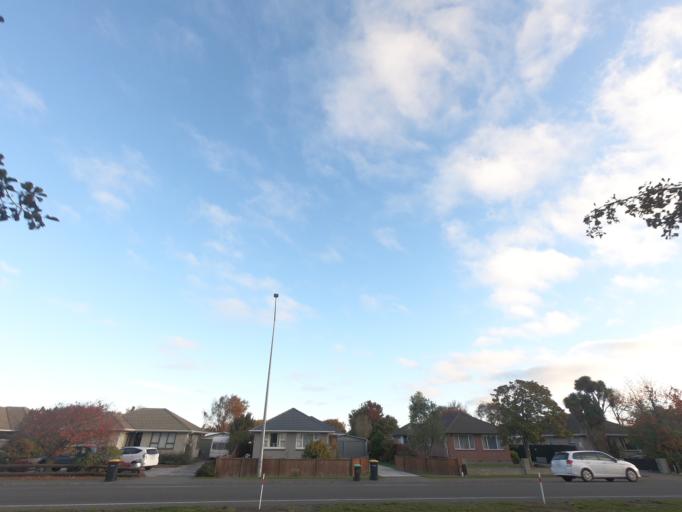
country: NZ
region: Canterbury
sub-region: Selwyn District
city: Prebbleton
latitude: -43.5694
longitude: 172.5653
